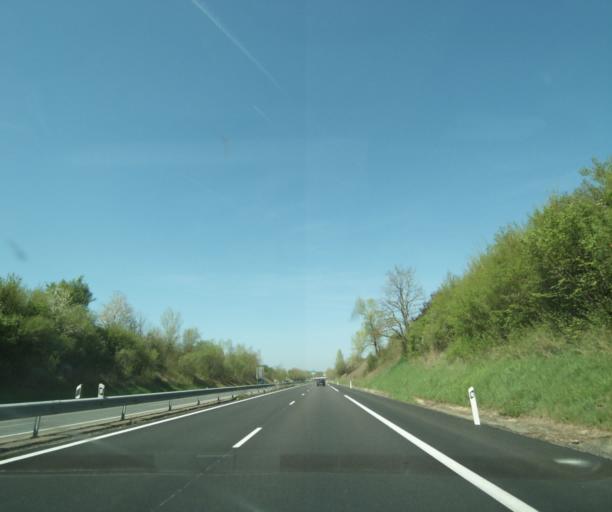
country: FR
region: Bourgogne
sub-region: Departement de la Nievre
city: La Charite-sur-Loire
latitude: 47.1982
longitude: 3.0209
